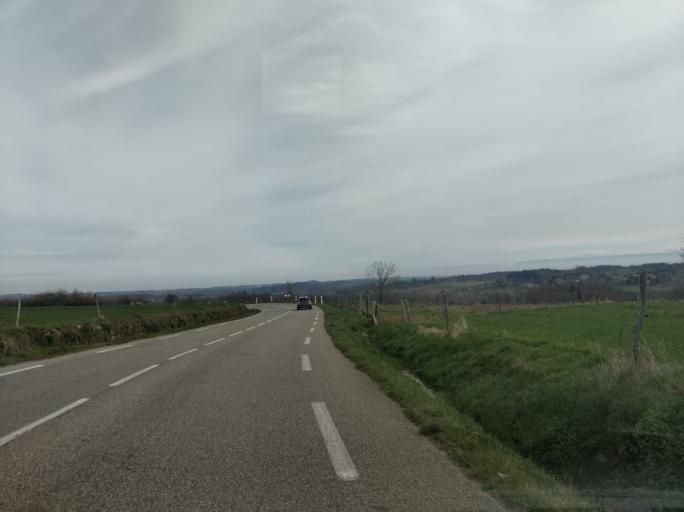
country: FR
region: Rhone-Alpes
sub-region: Departement de l'Ardeche
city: Roiffieux
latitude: 45.1988
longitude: 4.6530
